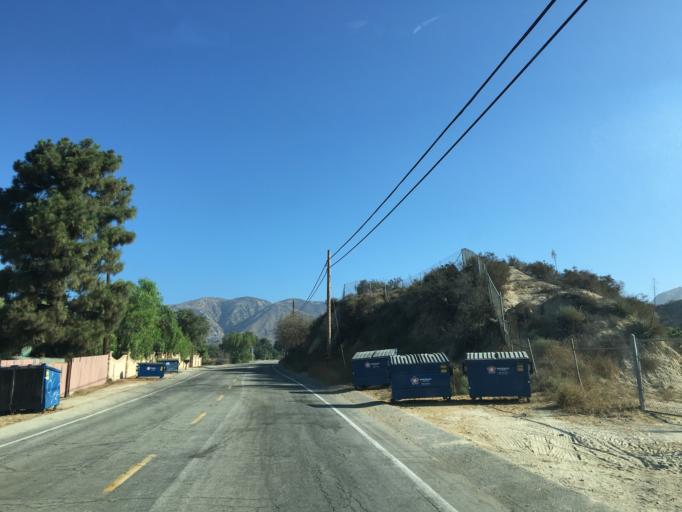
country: US
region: California
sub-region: Los Angeles County
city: San Fernando
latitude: 34.2997
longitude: -118.3759
